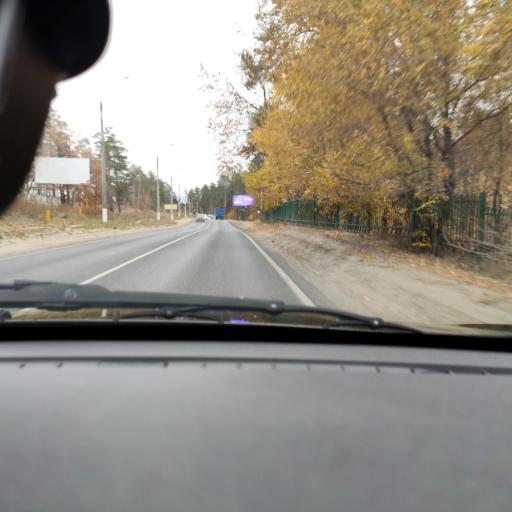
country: RU
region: Samara
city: Tol'yatti
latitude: 53.4853
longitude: 49.3149
